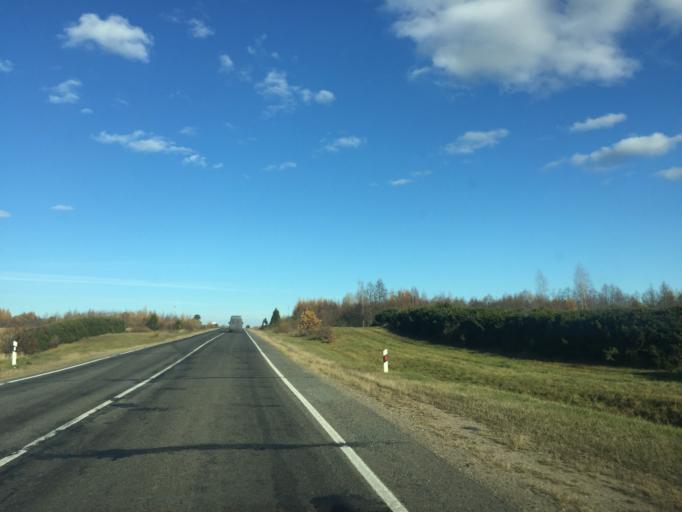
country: BY
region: Vitebsk
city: Dzisna
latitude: 55.2847
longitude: 28.1786
